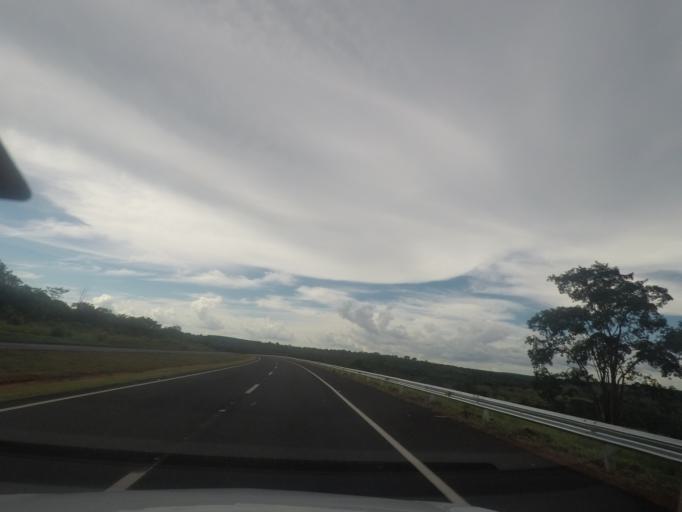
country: BR
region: Minas Gerais
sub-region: Prata
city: Prata
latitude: -19.4203
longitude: -48.8894
